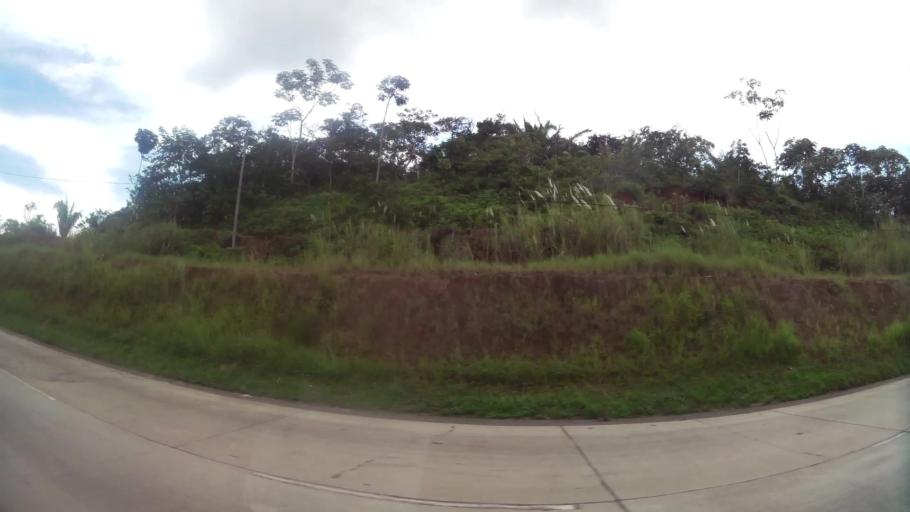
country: PA
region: Panama
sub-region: Distrito Arraijan
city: Arraijan
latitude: 8.9622
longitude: -79.6536
